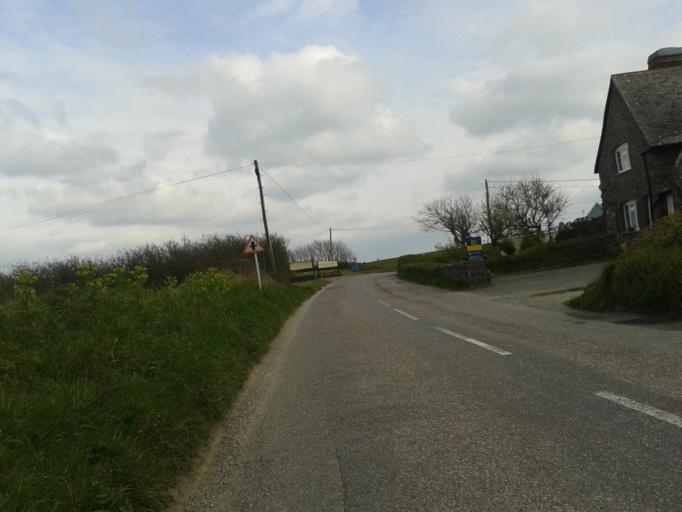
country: GB
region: England
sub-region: Devon
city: Braunton
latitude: 51.1793
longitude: -4.1820
